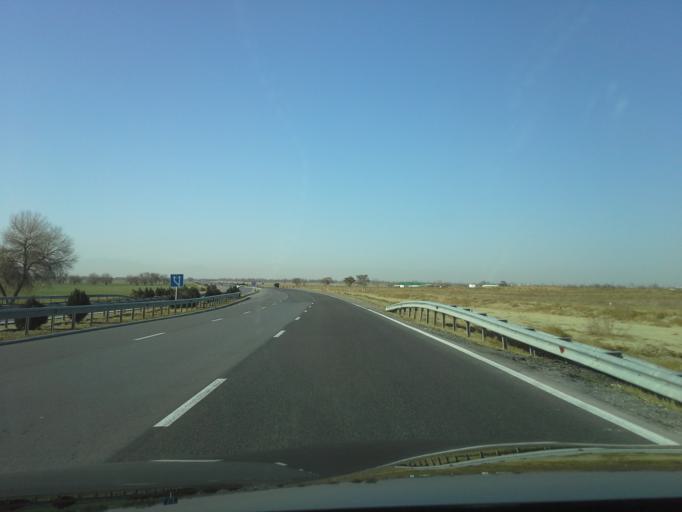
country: TM
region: Ahal
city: Annau
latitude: 37.8946
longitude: 58.6060
